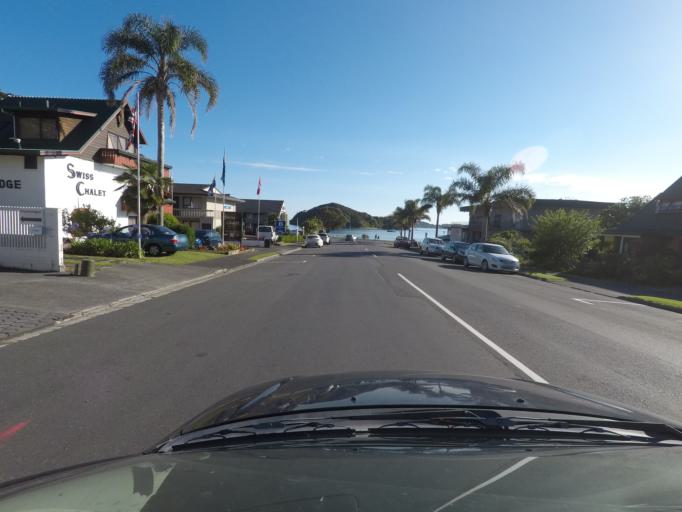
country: NZ
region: Northland
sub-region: Far North District
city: Paihia
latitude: -35.2806
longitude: 174.0892
